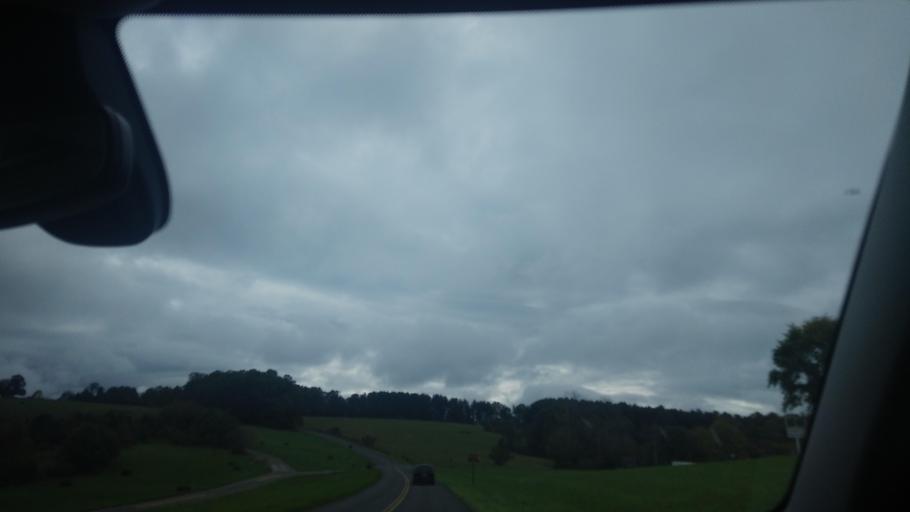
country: US
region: Virginia
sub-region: Carroll County
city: Cana
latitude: 36.6637
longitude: -80.6040
